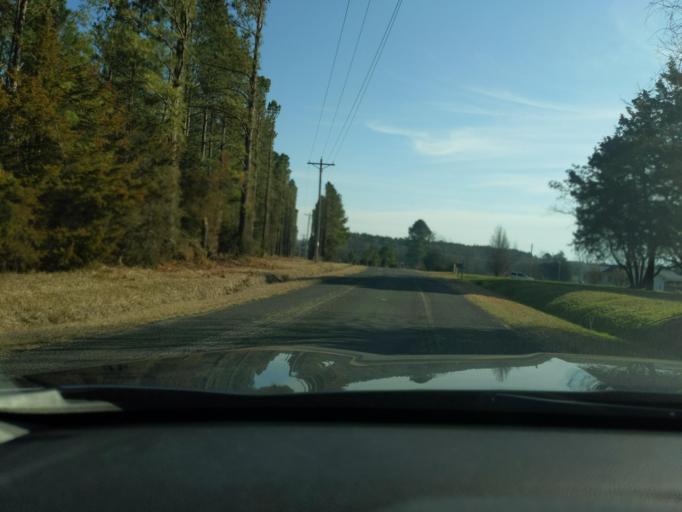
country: US
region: South Carolina
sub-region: Abbeville County
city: Calhoun Falls
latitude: 34.0812
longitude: -82.5695
